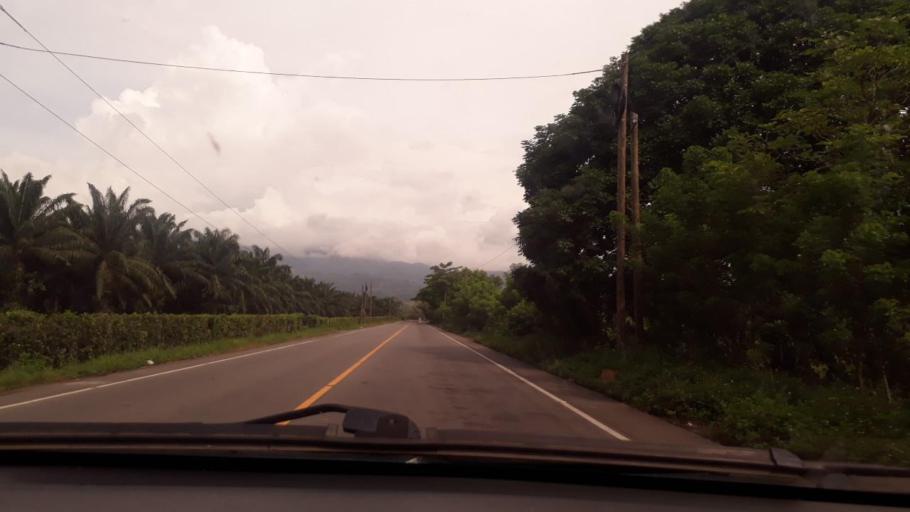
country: HN
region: Cortes
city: Potrerillos
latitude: 15.6116
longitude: -88.3946
